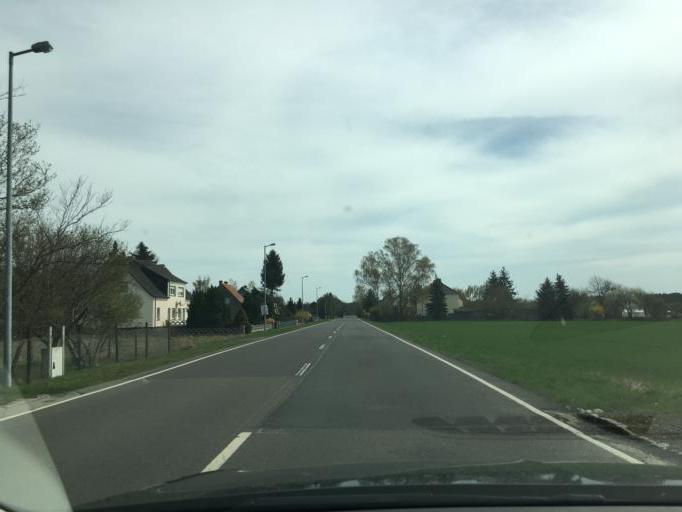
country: DE
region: Brandenburg
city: Tschernitz
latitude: 51.5733
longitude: 14.6222
